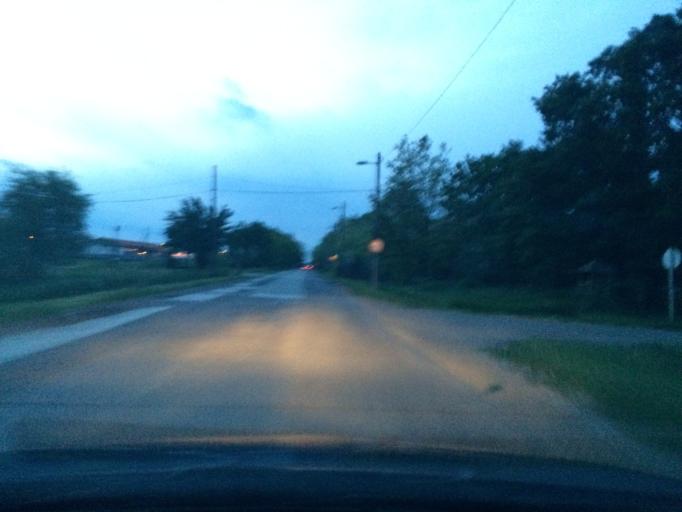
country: HU
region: Hajdu-Bihar
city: Hajdunanas
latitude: 47.9071
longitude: 21.4030
